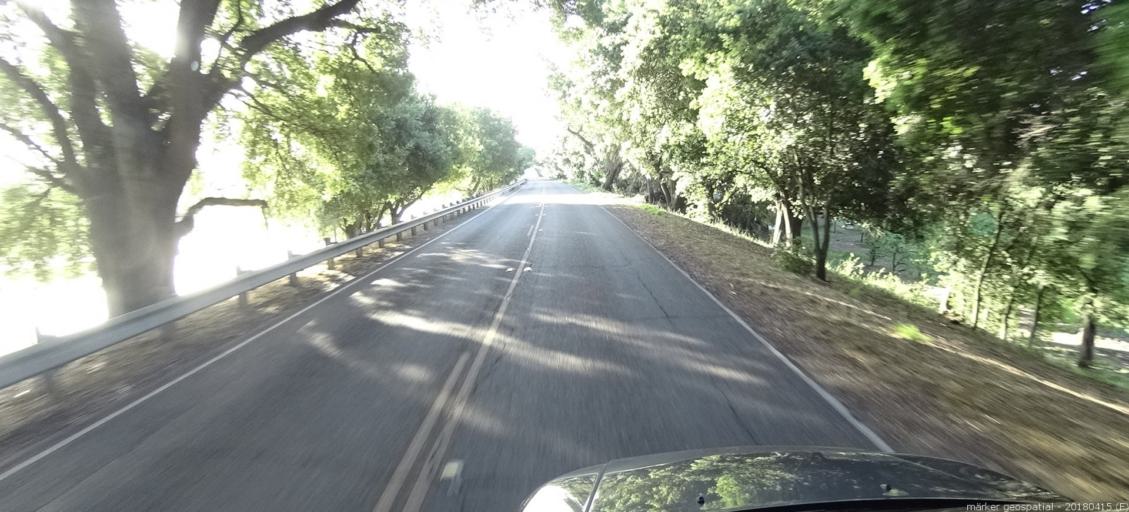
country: US
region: California
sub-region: Sacramento County
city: Walnut Grove
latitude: 38.2594
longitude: -121.5210
